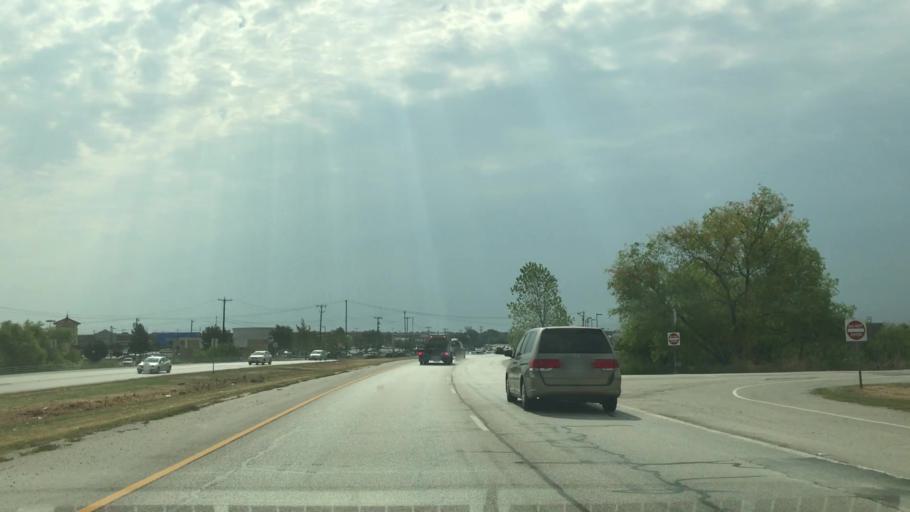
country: US
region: Texas
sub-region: Tarrant County
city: Watauga
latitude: 32.8948
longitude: -97.2926
